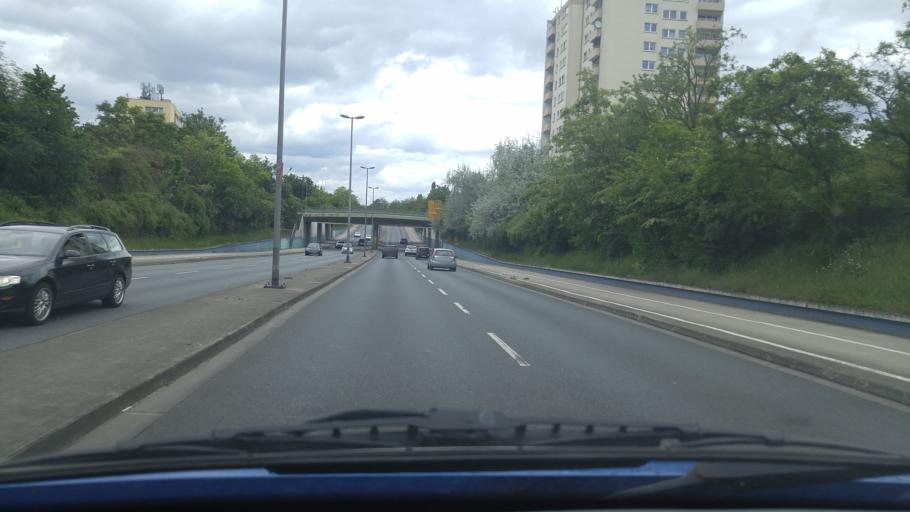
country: DE
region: Hesse
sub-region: Regierungsbezirk Darmstadt
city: Russelsheim
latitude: 49.9930
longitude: 8.4246
